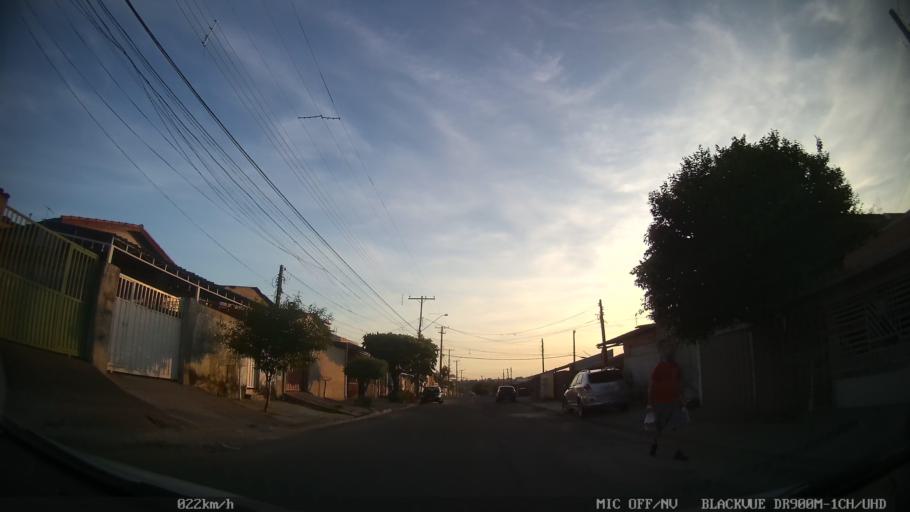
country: BR
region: Sao Paulo
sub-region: Campinas
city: Campinas
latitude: -22.9760
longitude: -47.1333
